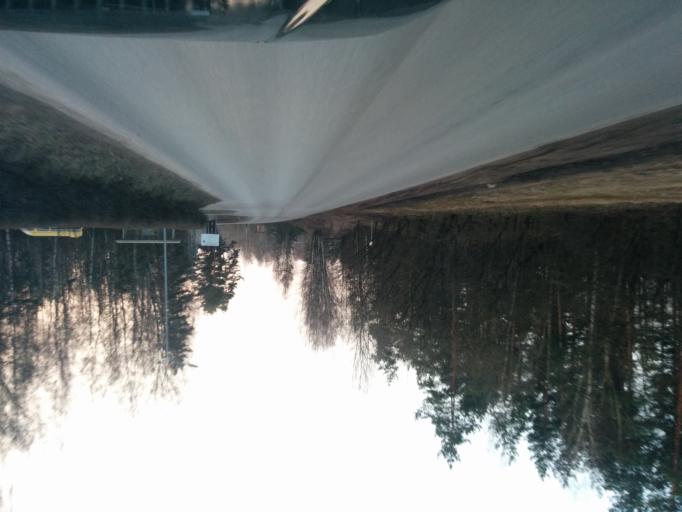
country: LV
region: Kekava
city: Balozi
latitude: 56.8709
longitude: 24.1113
